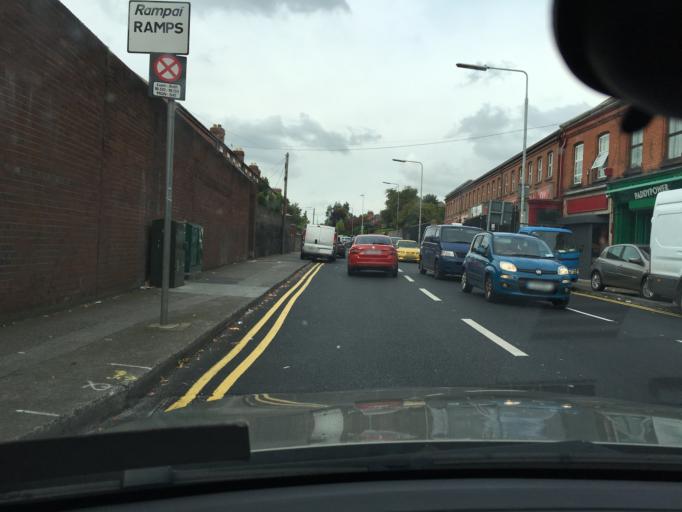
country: IE
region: Leinster
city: Cabra
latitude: 53.3574
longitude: -6.2891
